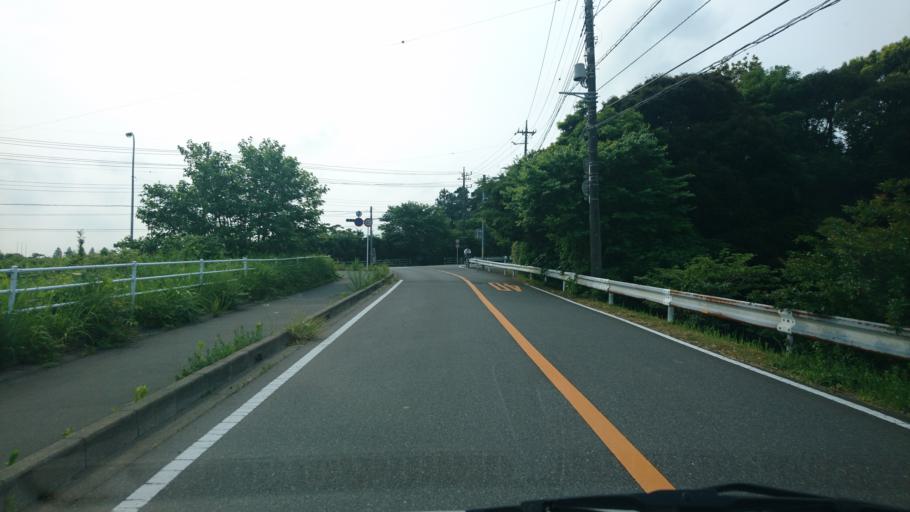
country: JP
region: Ibaraki
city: Edosaki
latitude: 35.8715
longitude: 140.3533
